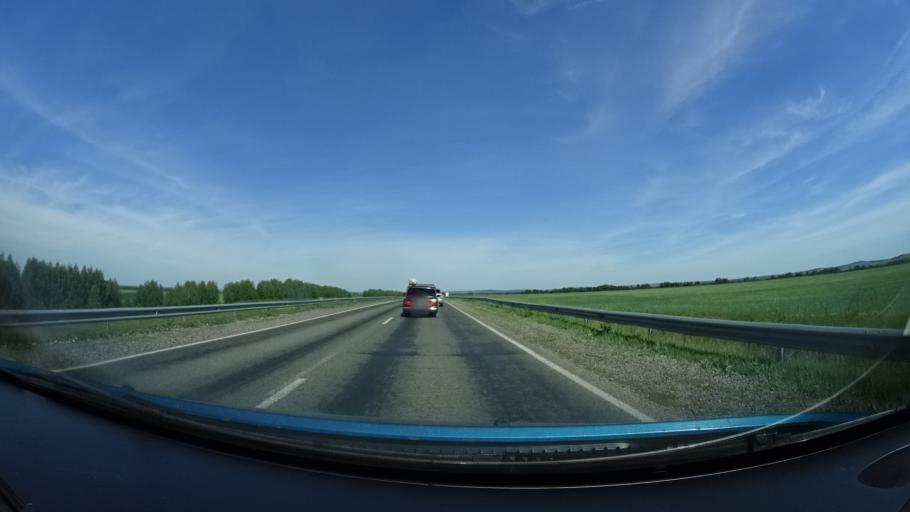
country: RU
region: Bashkortostan
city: Blagoveshchensk
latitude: 55.1945
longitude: 55.8351
